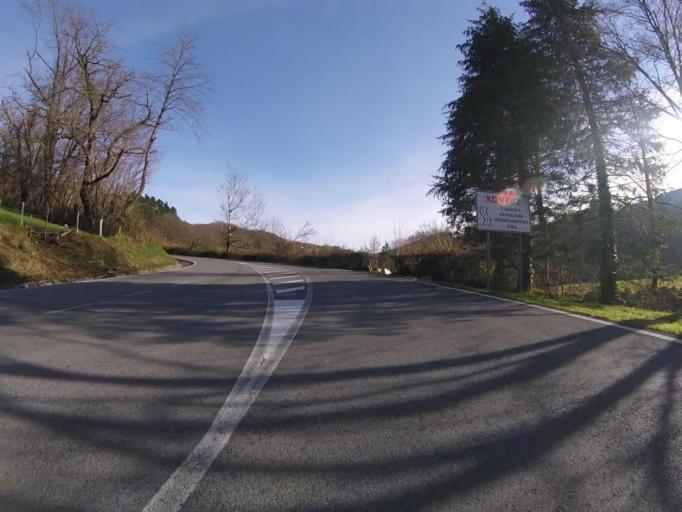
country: ES
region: Navarre
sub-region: Provincia de Navarra
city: Leitza
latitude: 43.0854
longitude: -1.9038
